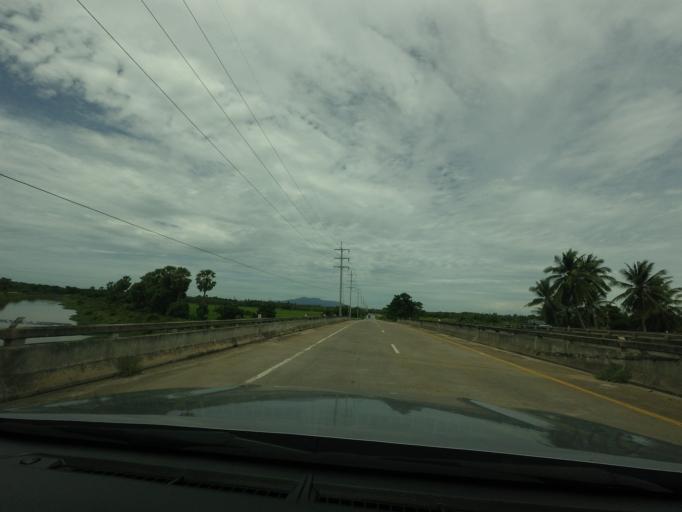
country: TH
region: Pattani
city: Pattani
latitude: 6.8356
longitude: 101.2217
